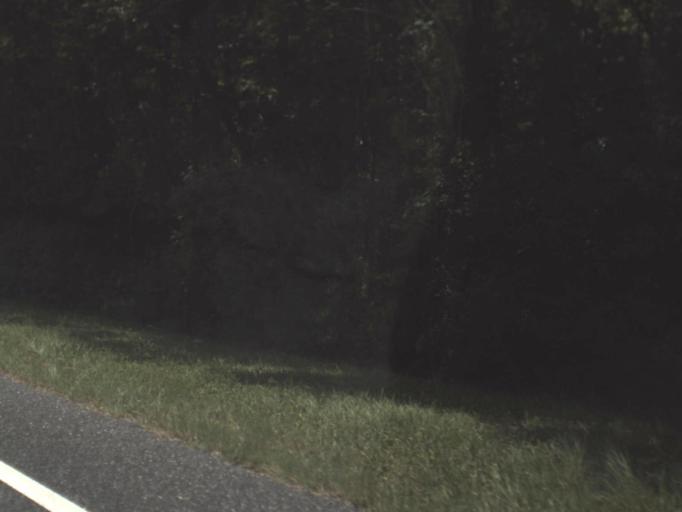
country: US
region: Florida
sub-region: Taylor County
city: Steinhatchee
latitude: 29.7027
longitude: -83.2868
